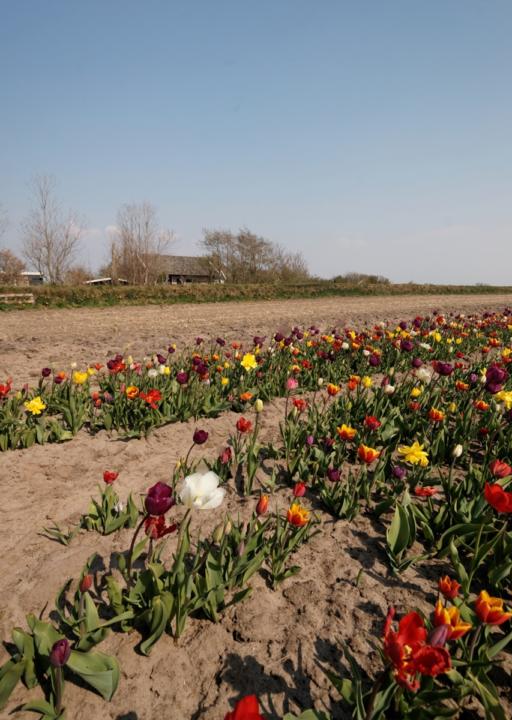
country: NL
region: North Holland
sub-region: Gemeente Texel
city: Den Burg
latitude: 53.0471
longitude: 4.7566
